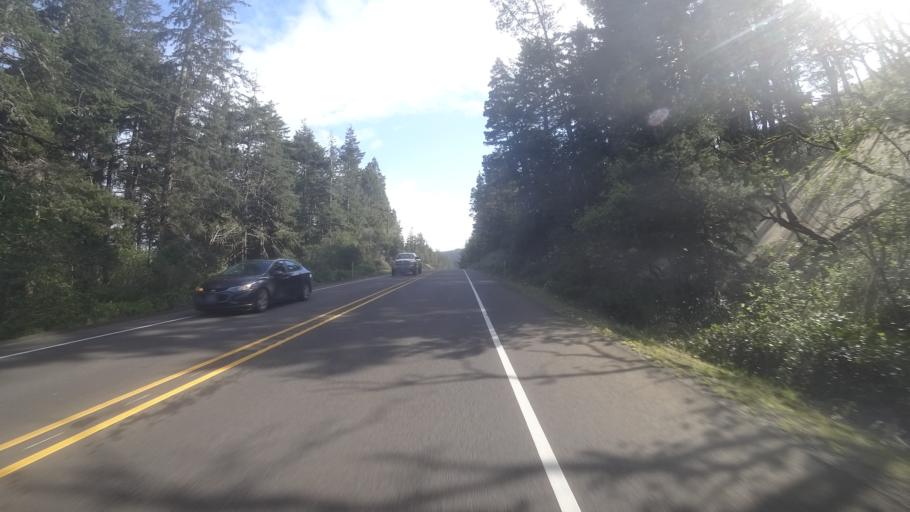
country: US
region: Oregon
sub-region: Lane County
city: Dunes City
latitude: 43.8940
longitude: -124.1184
